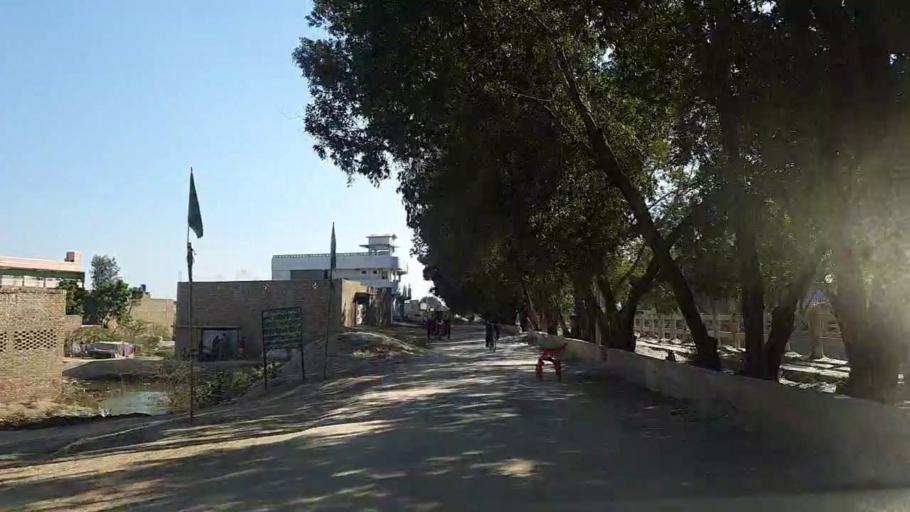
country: PK
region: Sindh
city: Nawabshah
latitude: 26.2496
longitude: 68.4205
